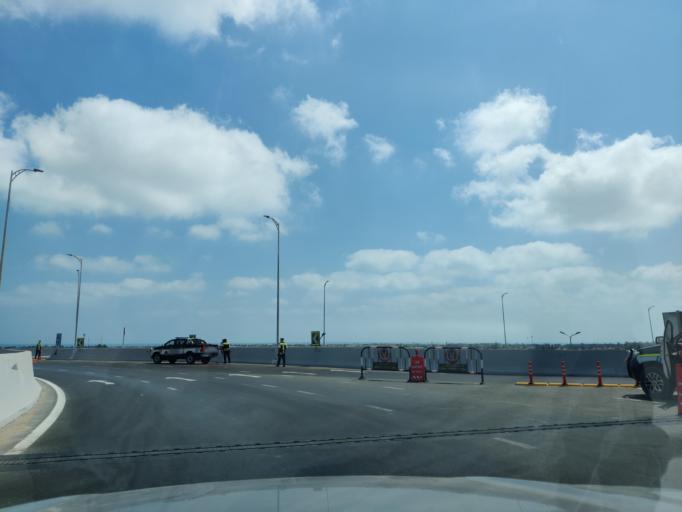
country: EG
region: Muhafazat Matruh
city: Al `Alamayn
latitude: 30.8386
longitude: 28.9540
